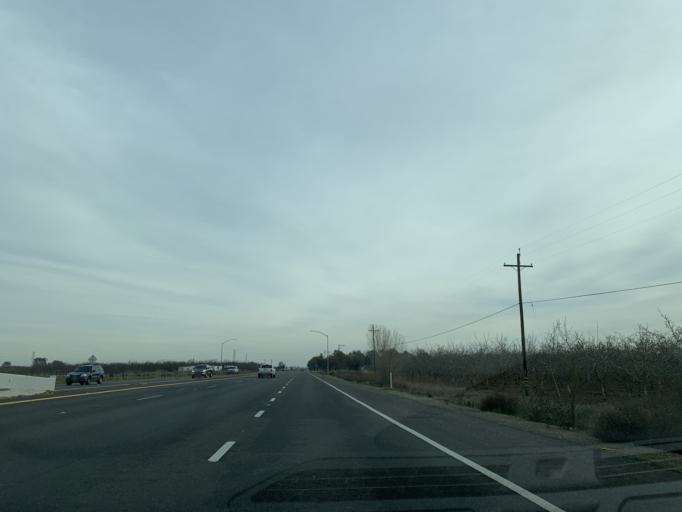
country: US
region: California
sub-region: Yuba County
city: Plumas Lake
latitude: 38.8962
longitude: -121.5815
